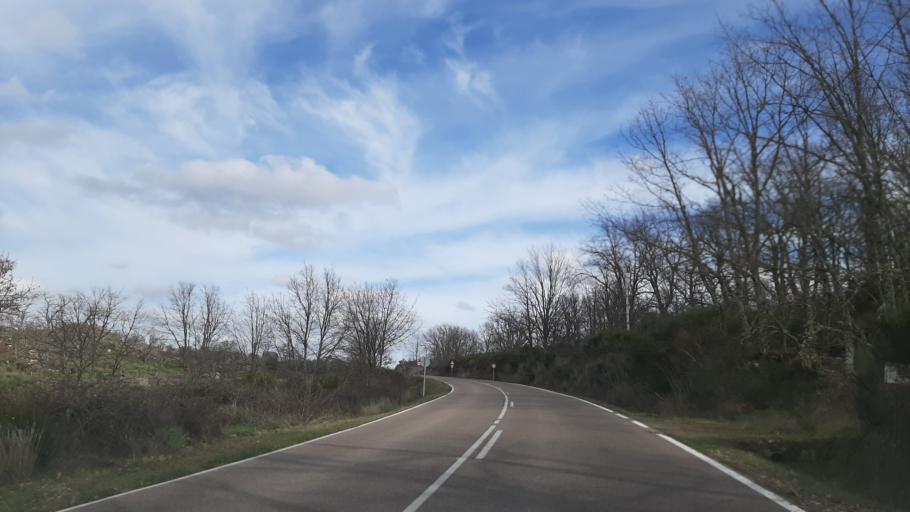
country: ES
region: Castille and Leon
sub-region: Provincia de Salamanca
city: Villarino de los Aires
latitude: 41.2622
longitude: -6.4300
